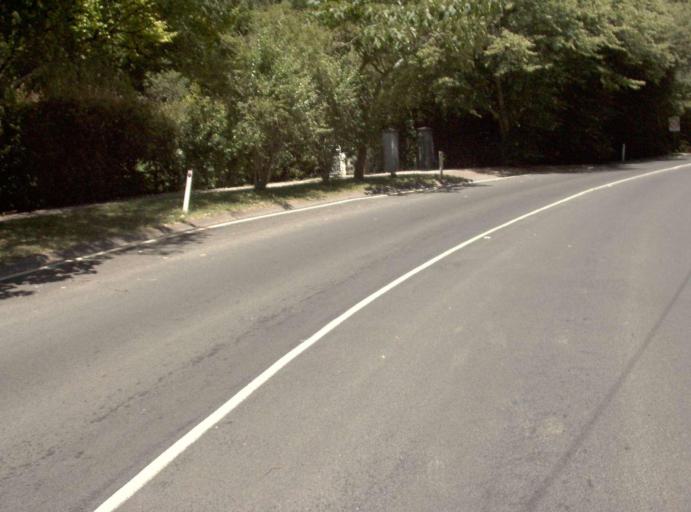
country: AU
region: Victoria
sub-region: Yarra Ranges
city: Olinda
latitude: -37.8452
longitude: 145.3608
